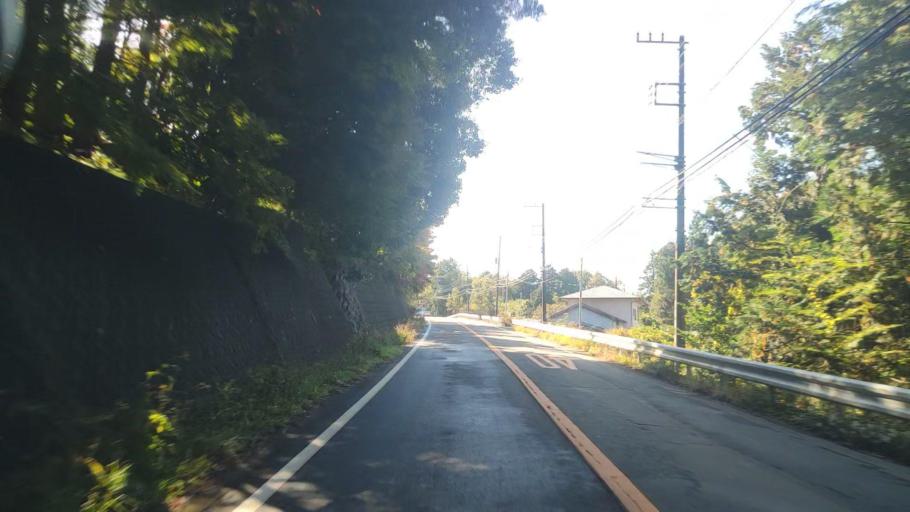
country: JP
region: Shizuoka
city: Atami
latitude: 35.0257
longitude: 139.0125
